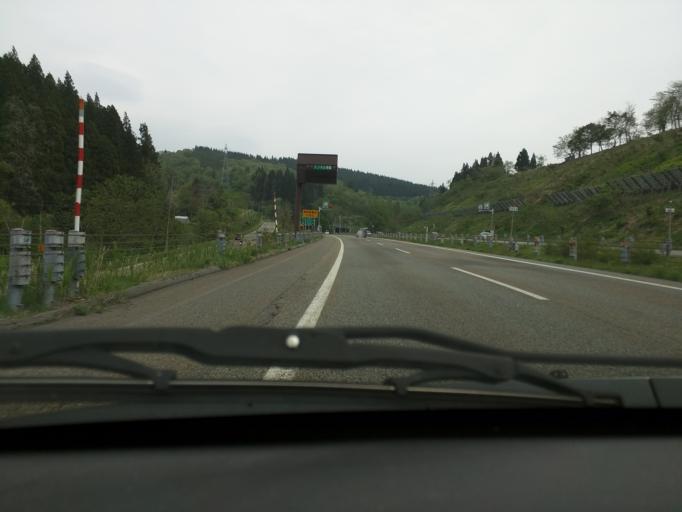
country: JP
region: Niigata
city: Ojiya
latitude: 37.2794
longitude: 138.7893
